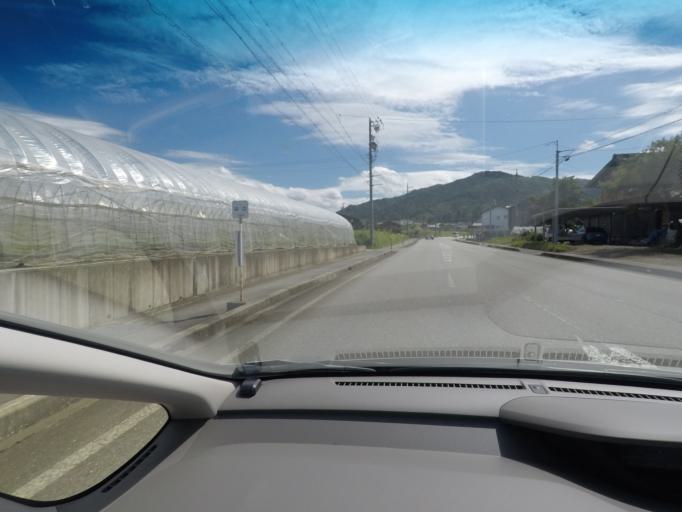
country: JP
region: Gifu
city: Takayama
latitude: 36.1360
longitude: 137.2911
